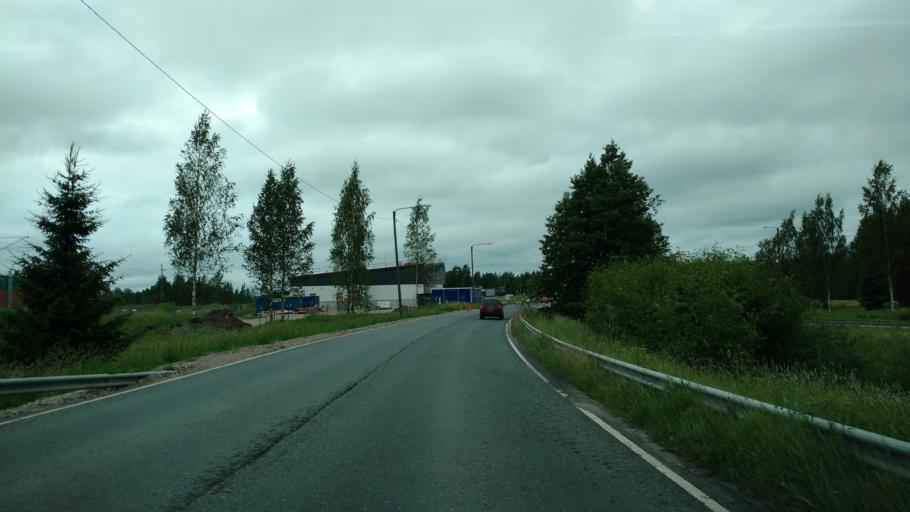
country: FI
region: Varsinais-Suomi
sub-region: Salo
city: Halikko
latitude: 60.3952
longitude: 23.0853
